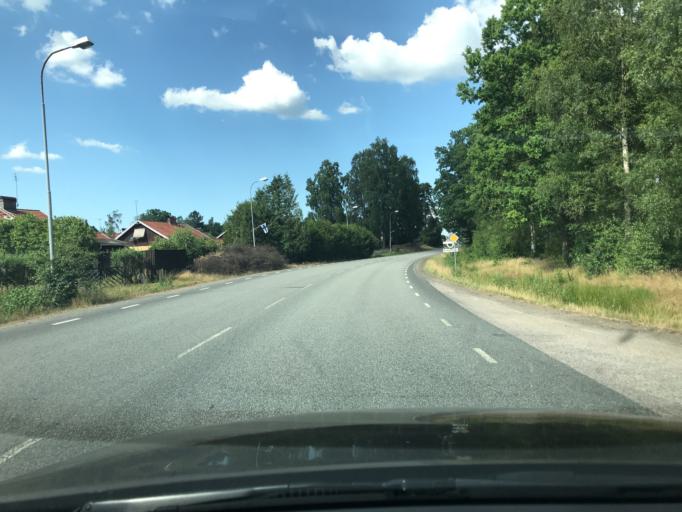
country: SE
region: Skane
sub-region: Hassleholms Kommun
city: Hastveda
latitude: 56.2805
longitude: 13.9329
